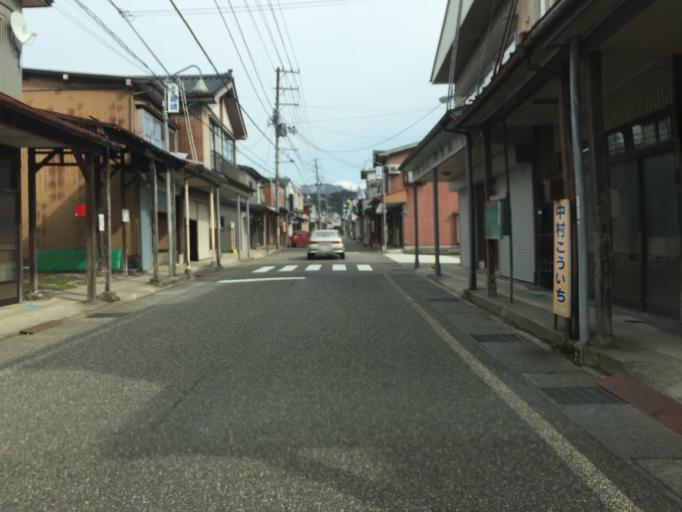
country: JP
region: Niigata
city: Tochio-honcho
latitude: 37.4715
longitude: 139.0008
